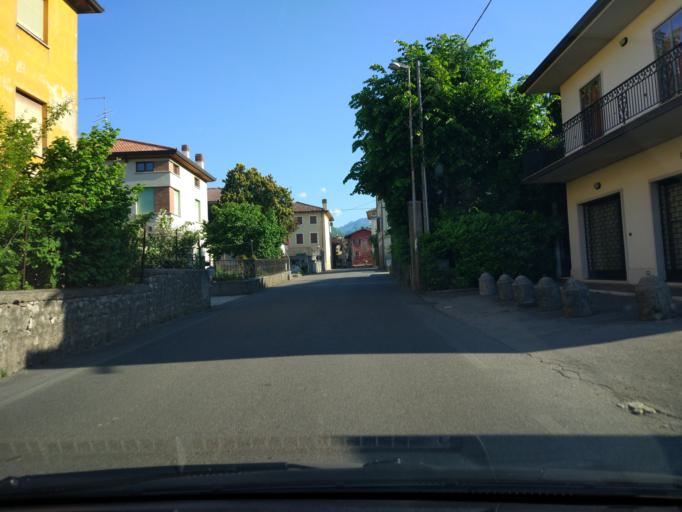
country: IT
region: Veneto
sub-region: Provincia di Verona
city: Badia Calavena
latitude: 45.5458
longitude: 11.1553
